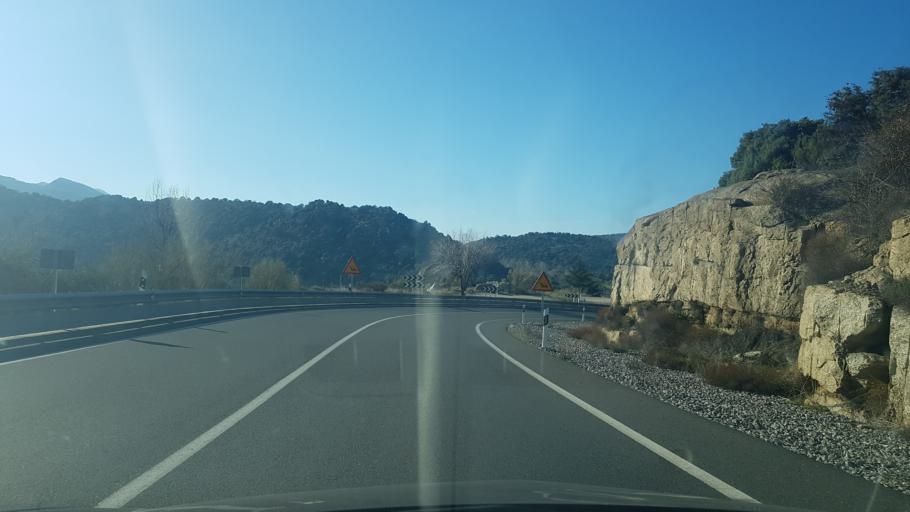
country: ES
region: Castille and Leon
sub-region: Provincia de Avila
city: El Tiemblo
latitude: 40.4379
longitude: -4.5606
